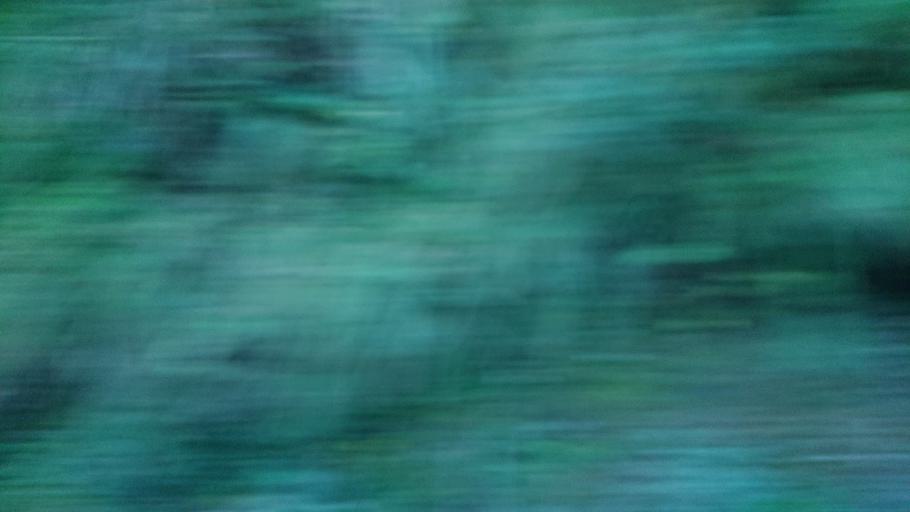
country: TW
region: Taiwan
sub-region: Yunlin
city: Douliu
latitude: 23.5307
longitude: 120.6530
